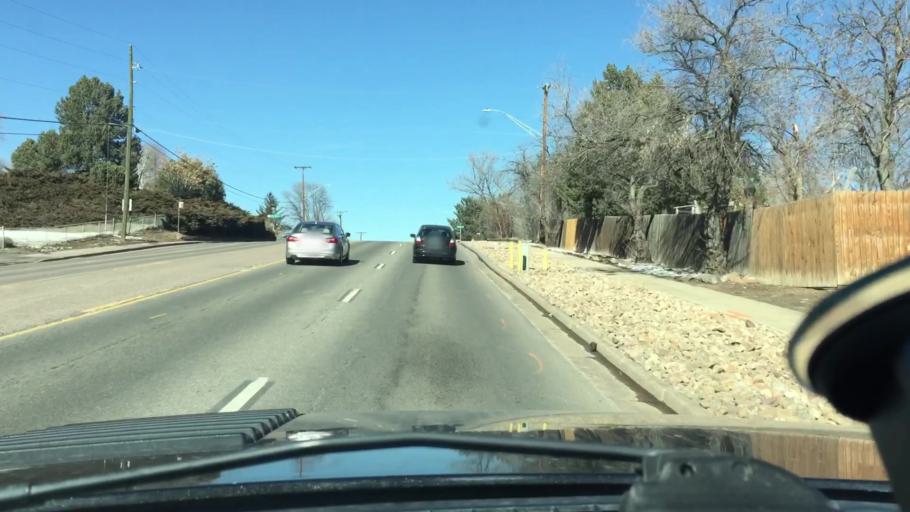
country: US
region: Colorado
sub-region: Adams County
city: Northglenn
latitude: 39.8746
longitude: -104.9966
